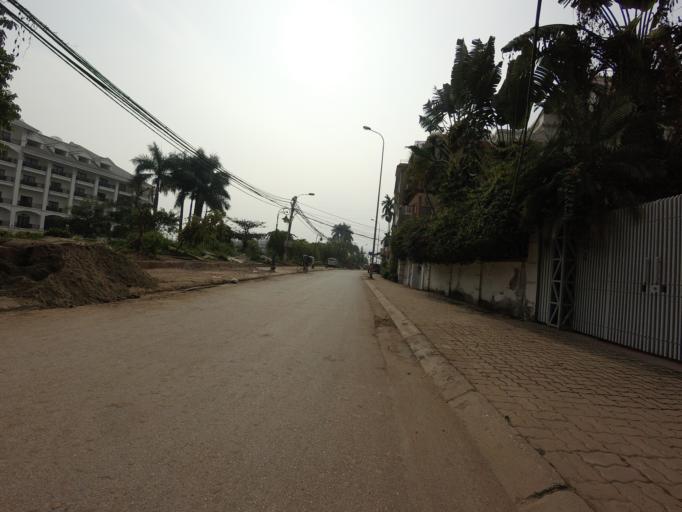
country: VN
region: Ha Noi
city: Tay Ho
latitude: 21.0588
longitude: 105.8308
